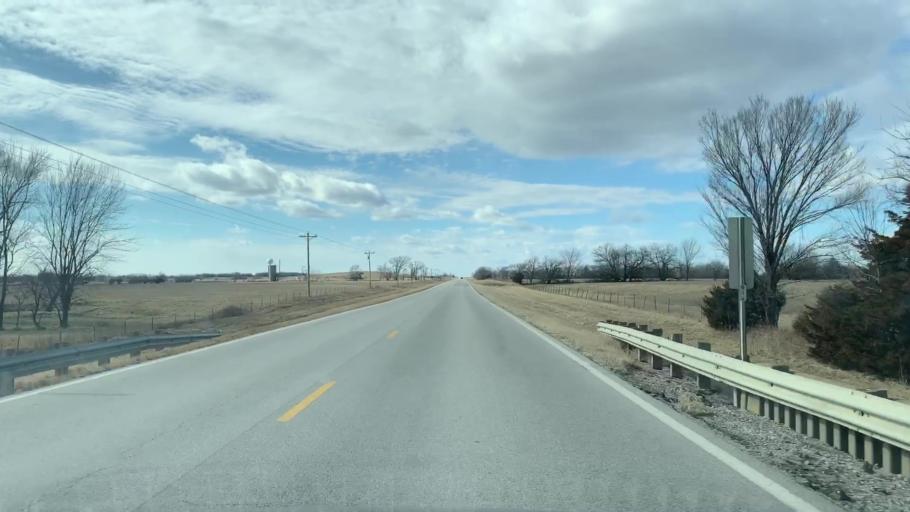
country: US
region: Kansas
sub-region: Neosho County
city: Erie
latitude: 37.5294
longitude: -95.3442
